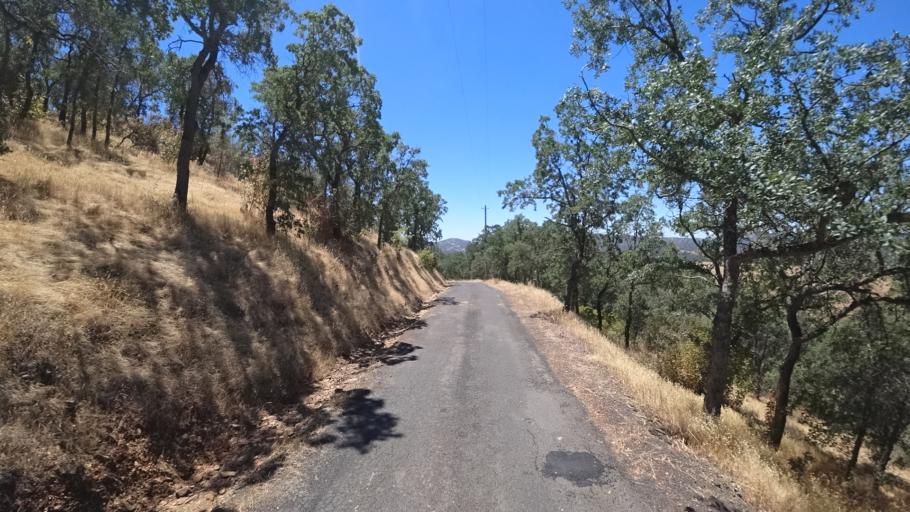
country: US
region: California
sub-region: Calaveras County
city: Copperopolis
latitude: 37.9920
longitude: -120.6683
